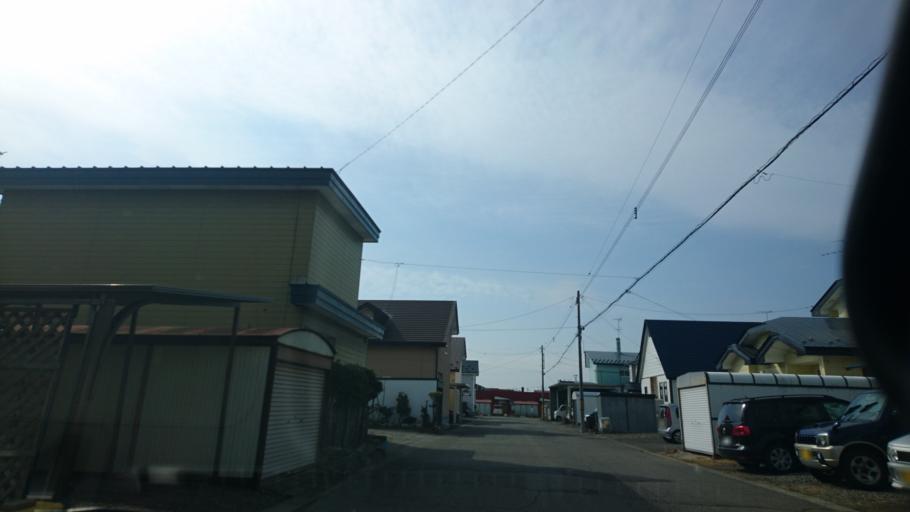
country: JP
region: Hokkaido
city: Otofuke
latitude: 42.9774
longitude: 143.2152
